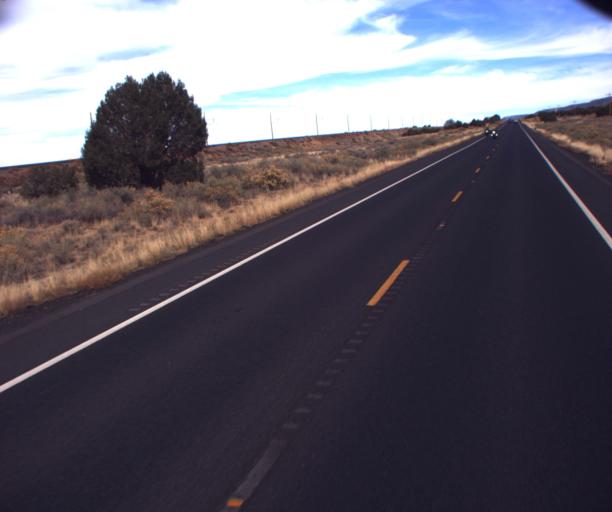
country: US
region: Arizona
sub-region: Coconino County
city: Kaibito
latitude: 36.4704
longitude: -110.6702
